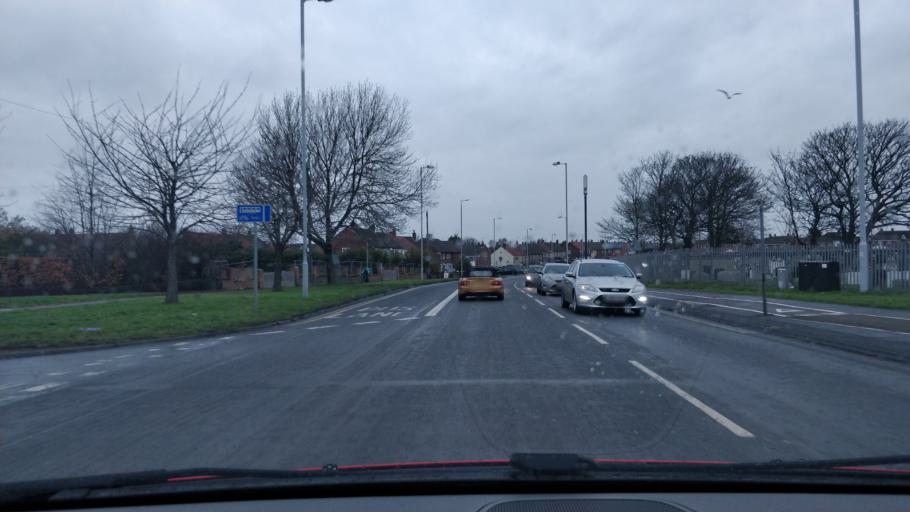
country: GB
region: England
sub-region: Sefton
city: Litherland
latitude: 53.4802
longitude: -2.9964
